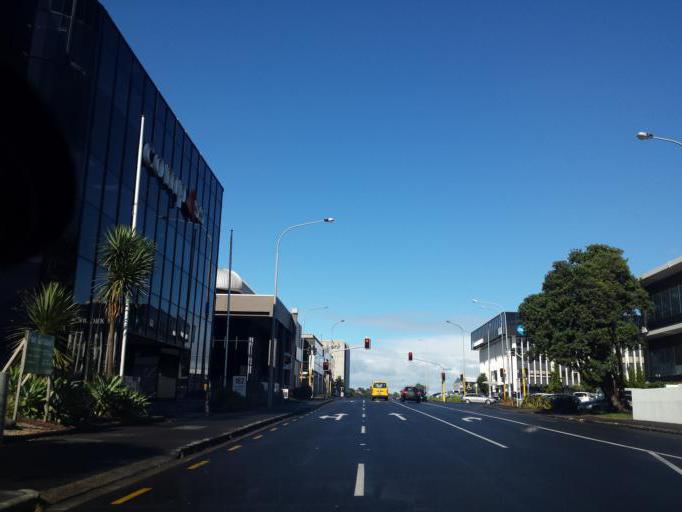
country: NZ
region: Auckland
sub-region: Auckland
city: Auckland
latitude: -36.8640
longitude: 174.7644
